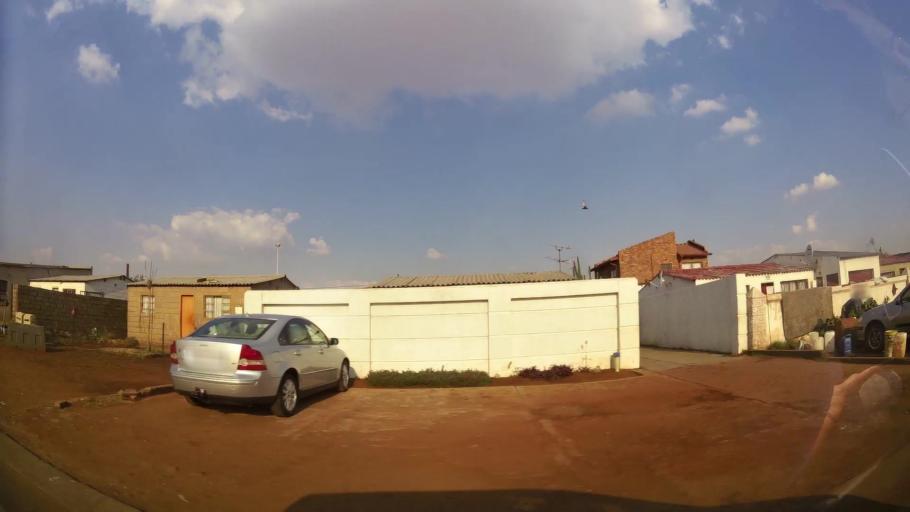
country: ZA
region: Gauteng
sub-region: Ekurhuleni Metropolitan Municipality
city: Germiston
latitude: -26.3503
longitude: 28.1889
